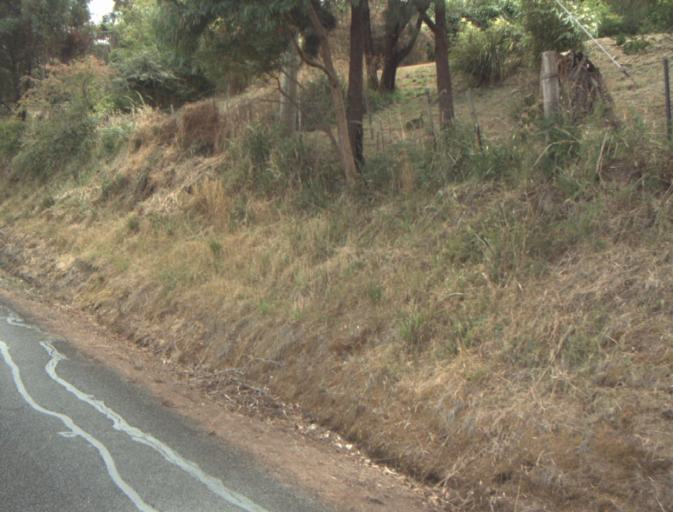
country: AU
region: Tasmania
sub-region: Launceston
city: Mayfield
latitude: -41.3137
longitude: 147.0423
